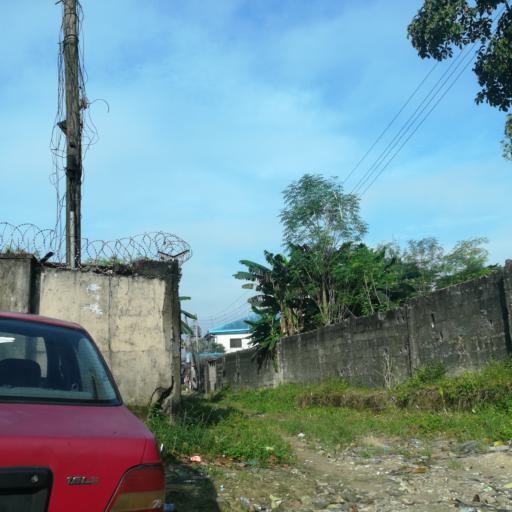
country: NG
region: Rivers
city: Port Harcourt
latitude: 4.8058
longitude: 7.0201
